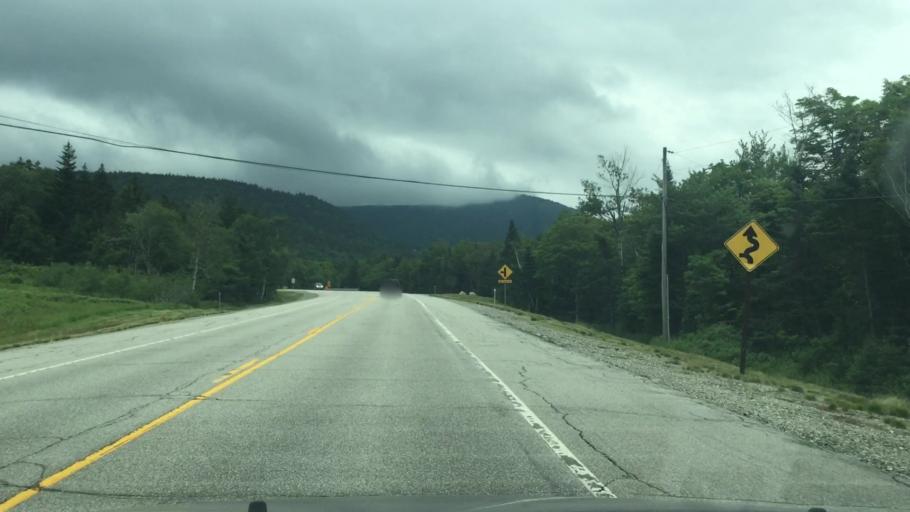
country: US
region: New Hampshire
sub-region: Grafton County
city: Deerfield
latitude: 44.2225
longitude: -71.4135
